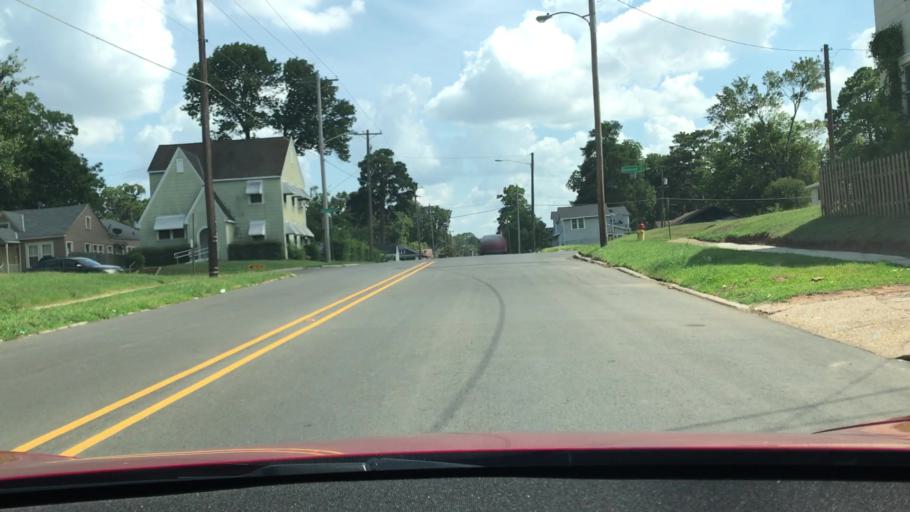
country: US
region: Louisiana
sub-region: Bossier Parish
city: Bossier City
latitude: 32.4900
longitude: -93.7332
